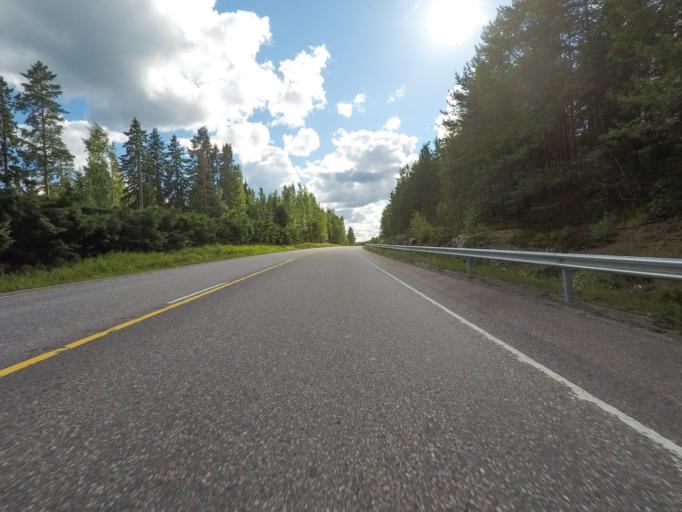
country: FI
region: Uusimaa
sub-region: Helsinki
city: Nurmijaervi
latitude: 60.5347
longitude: 24.6892
